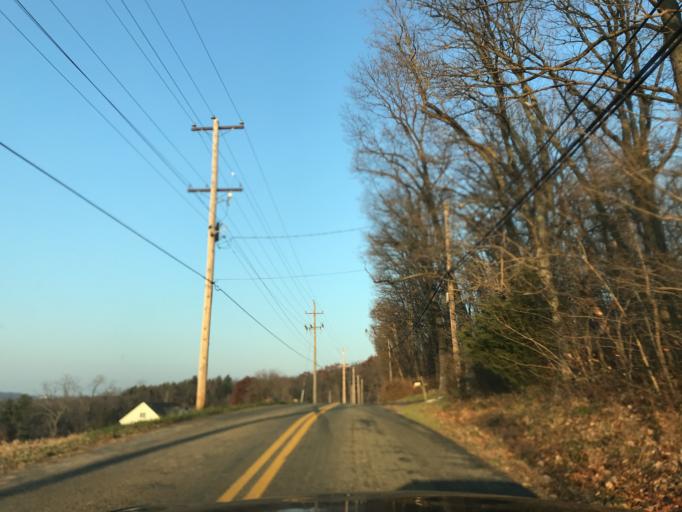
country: US
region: Pennsylvania
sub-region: York County
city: Susquehanna Trails
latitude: 39.6938
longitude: -76.3661
